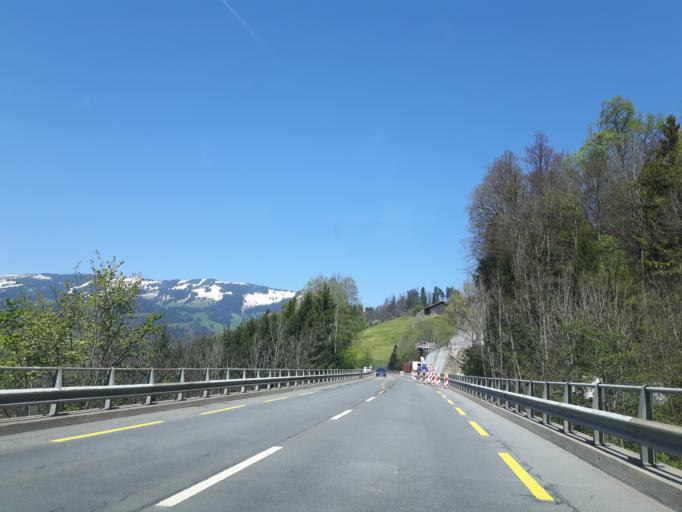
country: CH
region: Schwyz
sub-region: Bezirk Schwyz
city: Steinen
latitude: 47.0501
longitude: 8.6293
